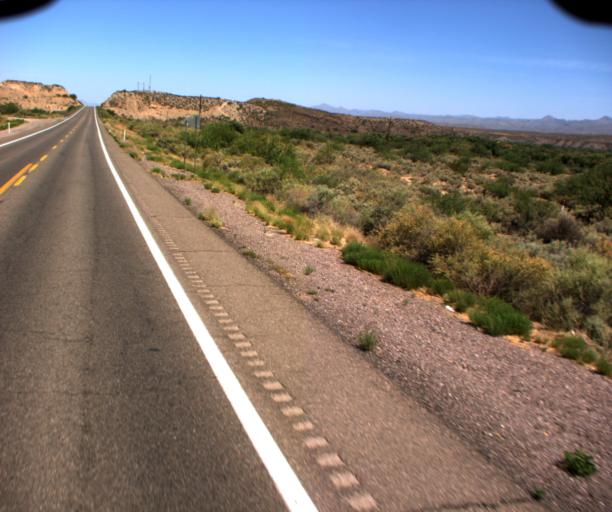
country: US
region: Arizona
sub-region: Graham County
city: Bylas
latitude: 33.1001
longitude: -110.0794
